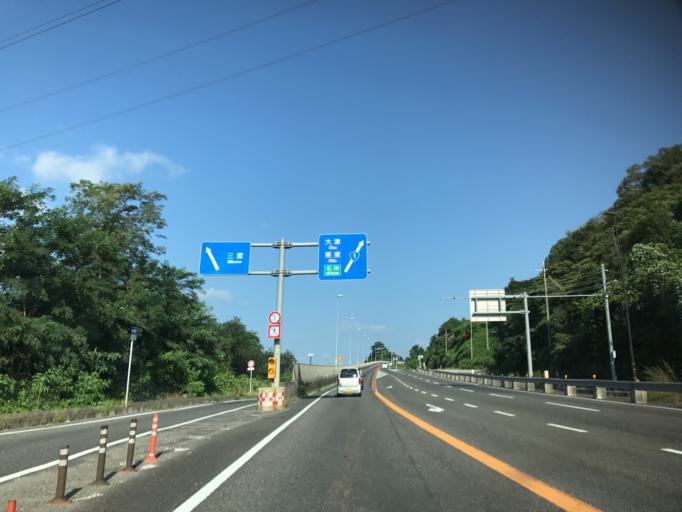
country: JP
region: Shiga Prefecture
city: Minakuchicho-matoba
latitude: 34.9853
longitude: 136.1244
